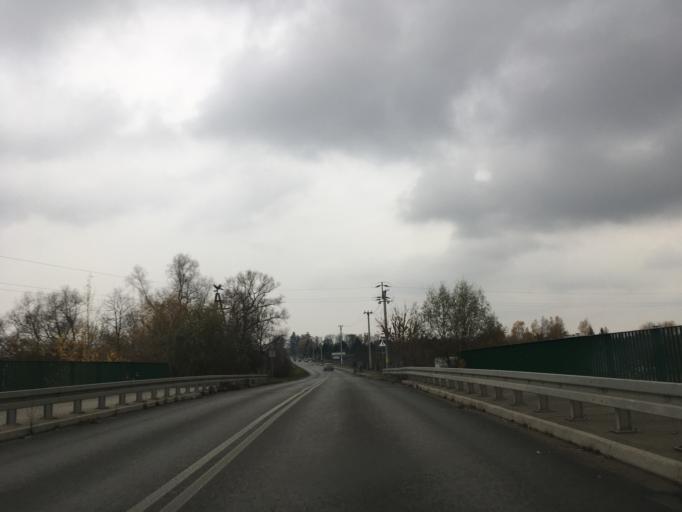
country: PL
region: Masovian Voivodeship
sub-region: Powiat piaseczynski
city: Zalesie Gorne
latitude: 52.0463
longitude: 21.0050
